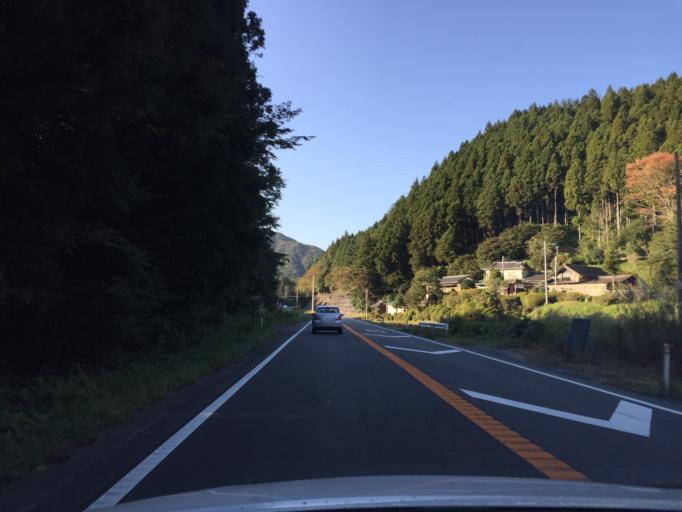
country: JP
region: Fukushima
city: Iwaki
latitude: 37.0793
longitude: 140.7836
